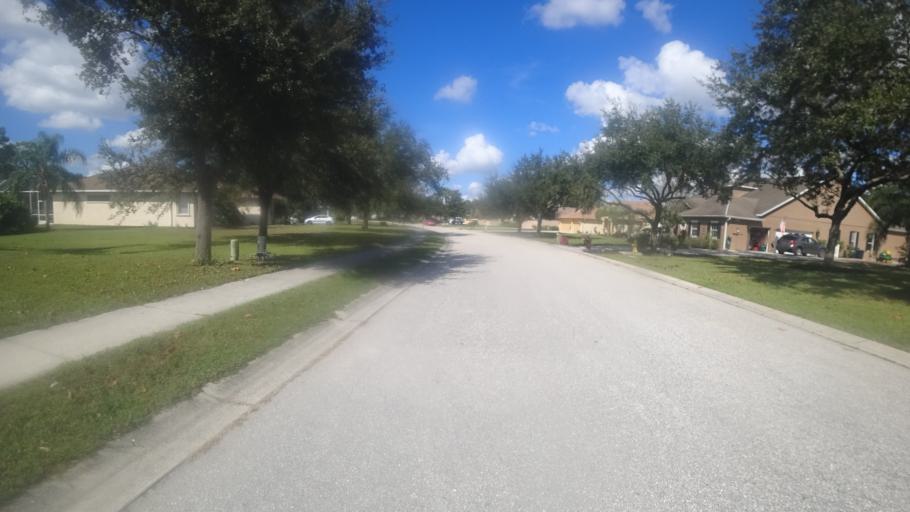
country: US
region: Florida
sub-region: Manatee County
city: Ellenton
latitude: 27.5019
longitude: -82.3998
